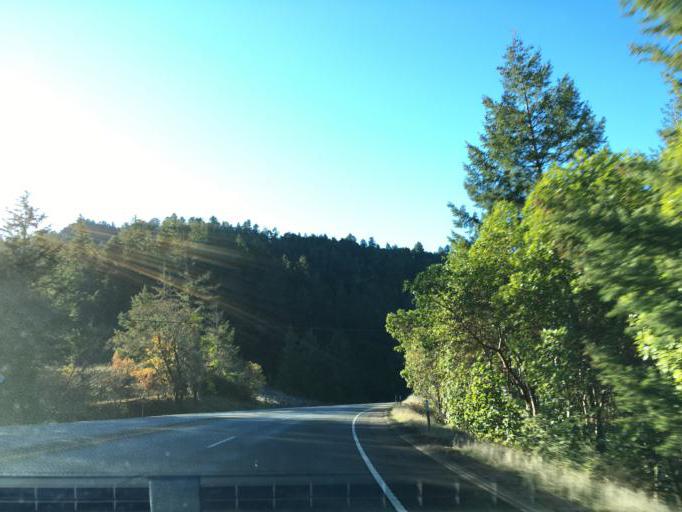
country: US
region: California
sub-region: Mendocino County
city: Laytonville
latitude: 39.8278
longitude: -123.6064
